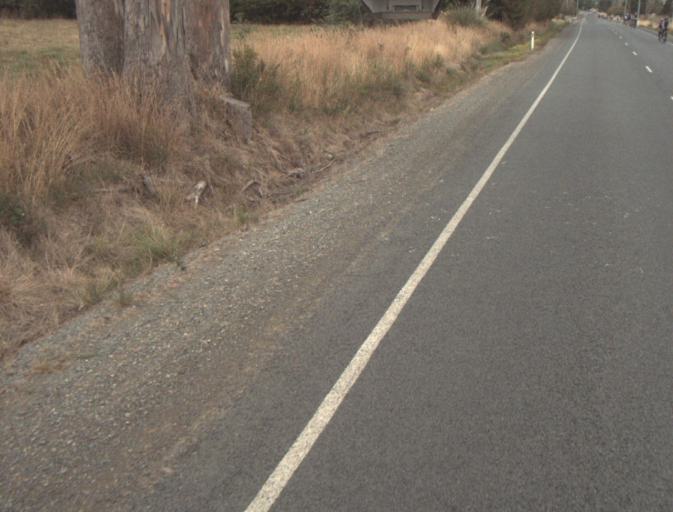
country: AU
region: Tasmania
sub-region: Launceston
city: Mayfield
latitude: -41.2397
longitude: 147.2159
